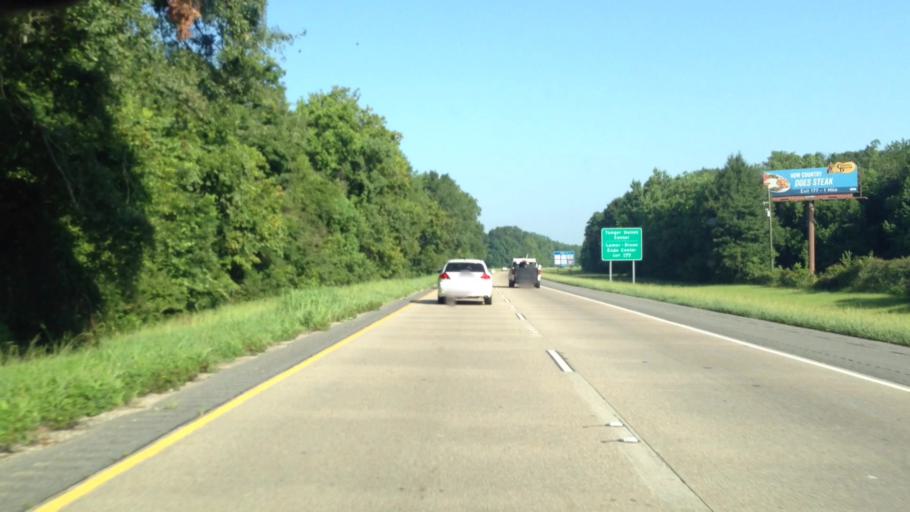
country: US
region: Louisiana
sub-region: Ascension Parish
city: Gonzales
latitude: 30.1987
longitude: -90.9325
